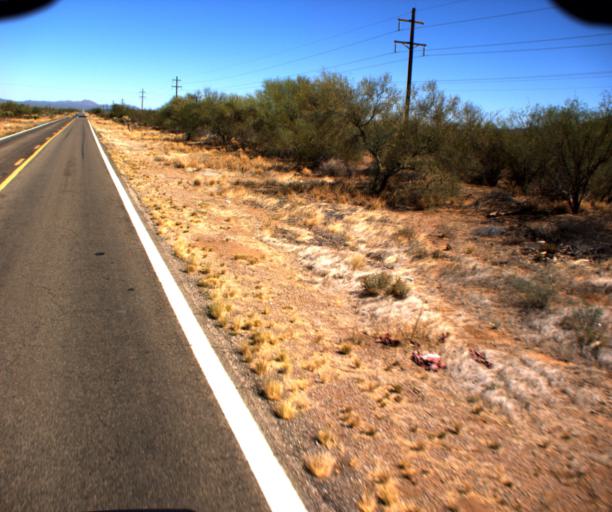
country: US
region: Arizona
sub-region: Pima County
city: Sells
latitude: 32.0122
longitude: -111.9950
